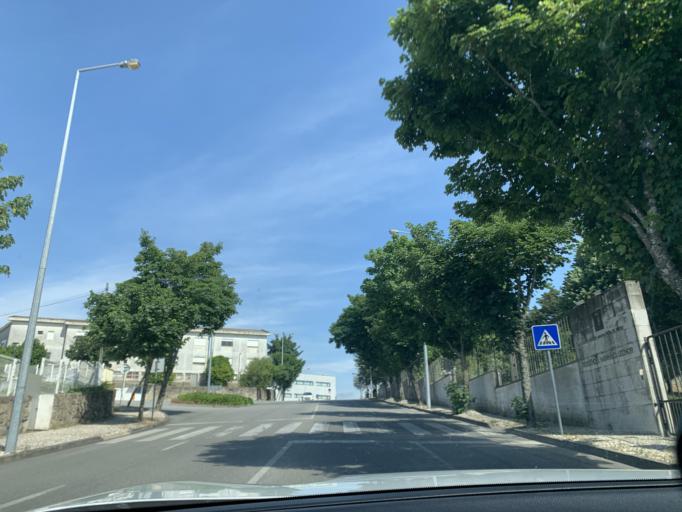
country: PT
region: Viseu
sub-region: Viseu
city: Viseu
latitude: 40.6526
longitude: -7.9050
